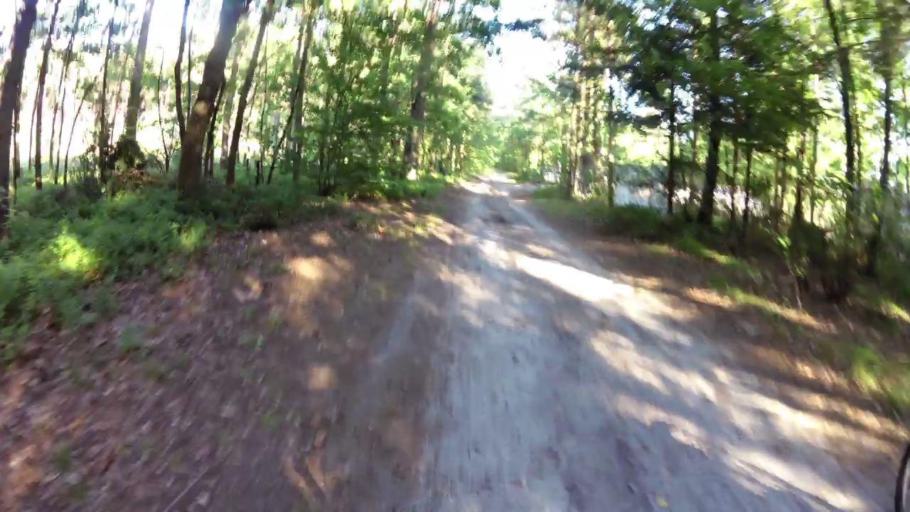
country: PL
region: West Pomeranian Voivodeship
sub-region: Powiat bialogardzki
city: Tychowo
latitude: 53.9478
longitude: 16.1215
